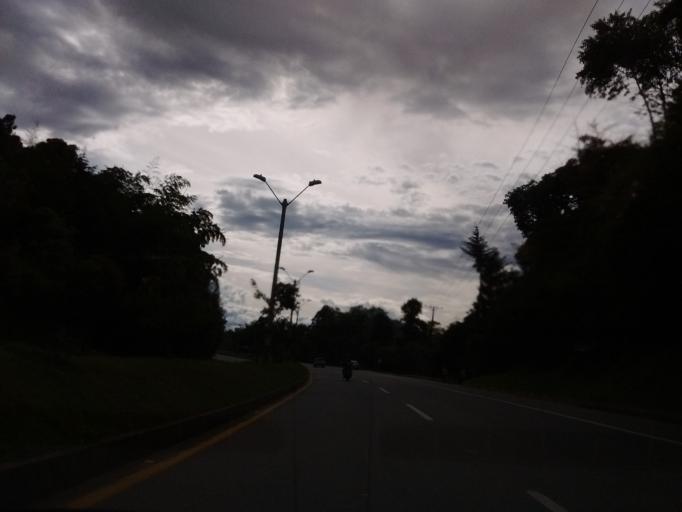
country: CO
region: Antioquia
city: Santuario
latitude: 6.1371
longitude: -75.2801
